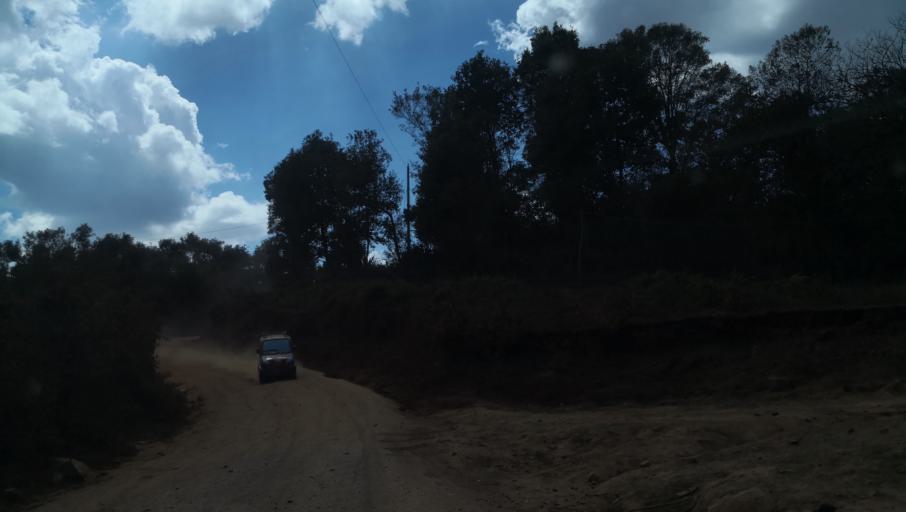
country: GT
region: Jalapa
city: San Carlos Alzatate
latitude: 14.4000
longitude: -89.9905
